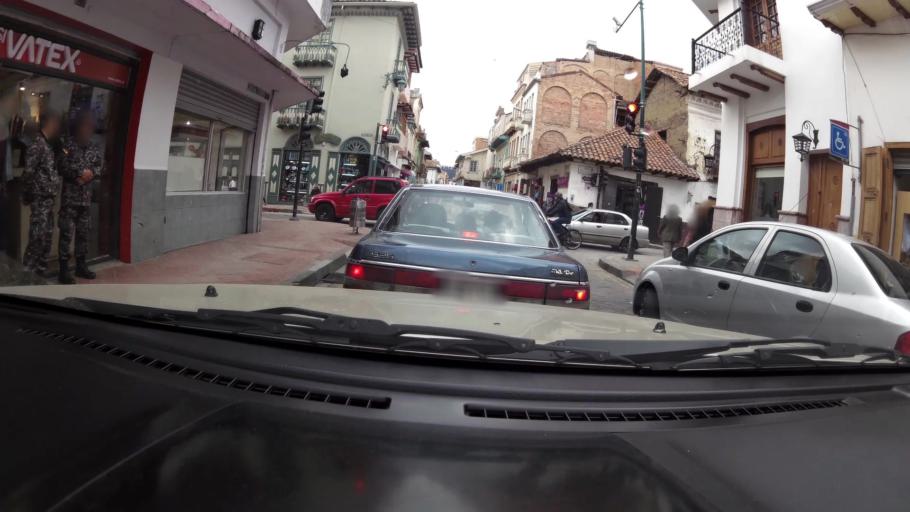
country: EC
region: Azuay
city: Cuenca
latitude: -2.8971
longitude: -79.0070
